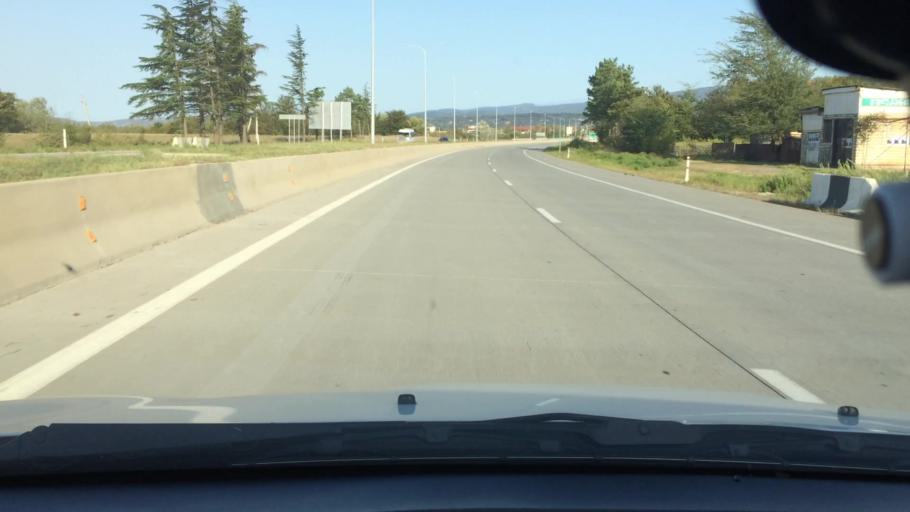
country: GE
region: Imereti
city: Zestap'oni
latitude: 42.1657
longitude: 42.9403
